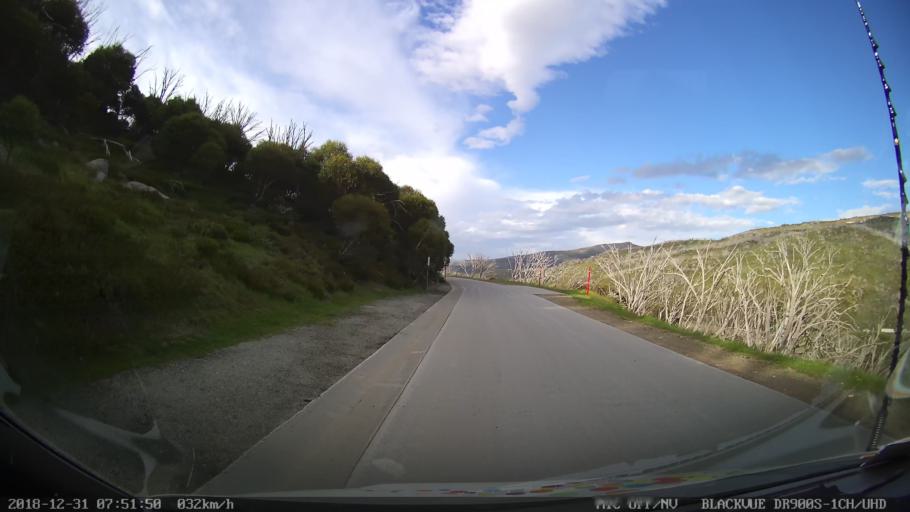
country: AU
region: New South Wales
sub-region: Snowy River
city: Jindabyne
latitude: -36.3782
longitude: 148.3746
